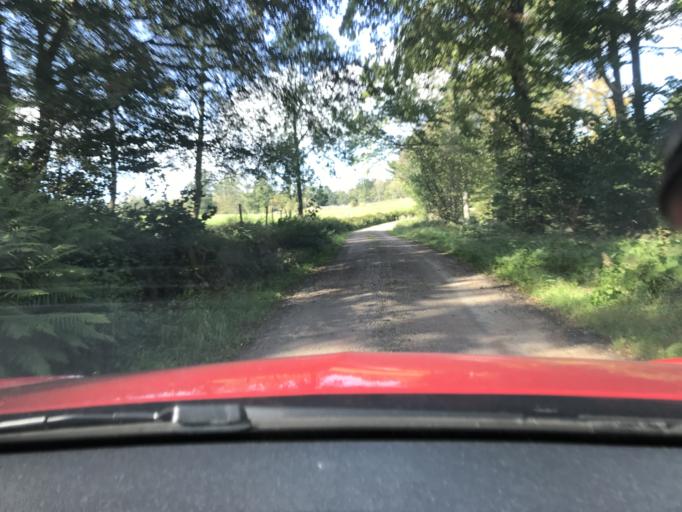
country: SE
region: Skane
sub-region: Hassleholms Kommun
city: Sosdala
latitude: 55.9997
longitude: 13.7049
